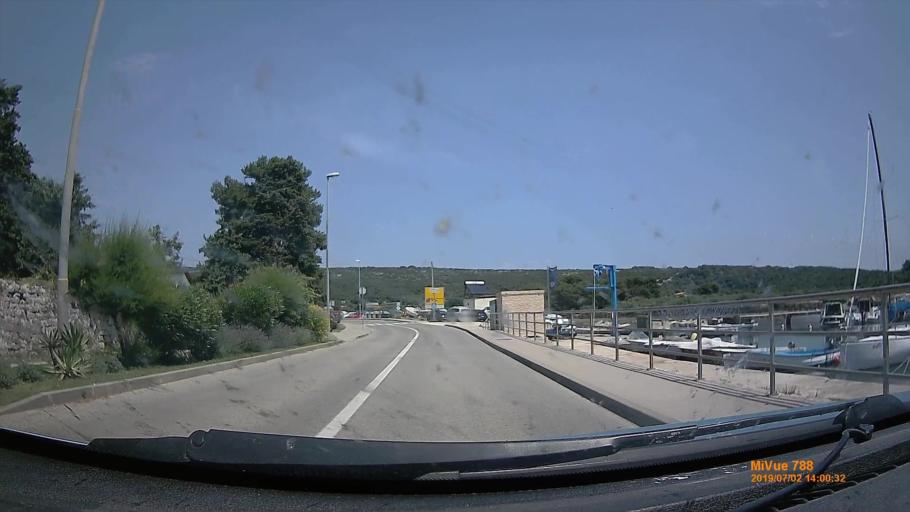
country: HR
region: Primorsko-Goranska
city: Mali Losinj
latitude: 44.6933
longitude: 14.3943
